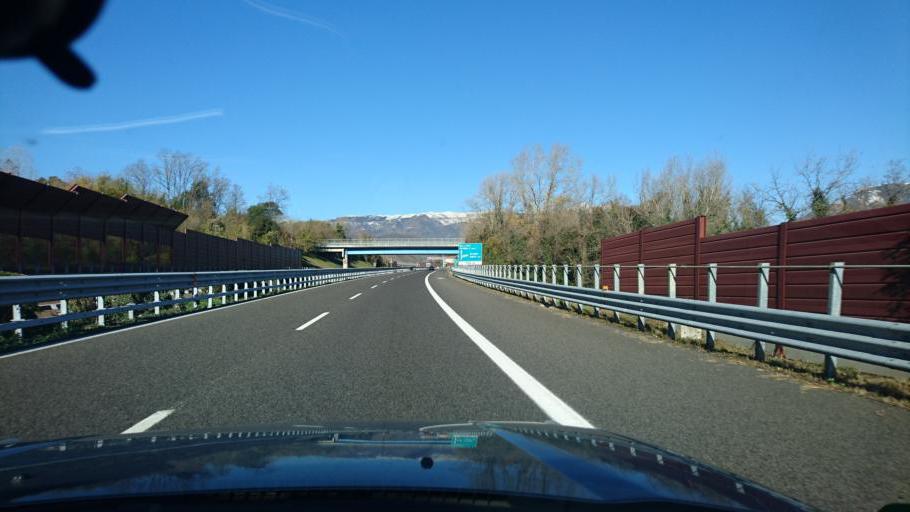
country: IT
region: Veneto
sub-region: Provincia di Treviso
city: Carpesica
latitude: 45.9537
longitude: 12.2932
